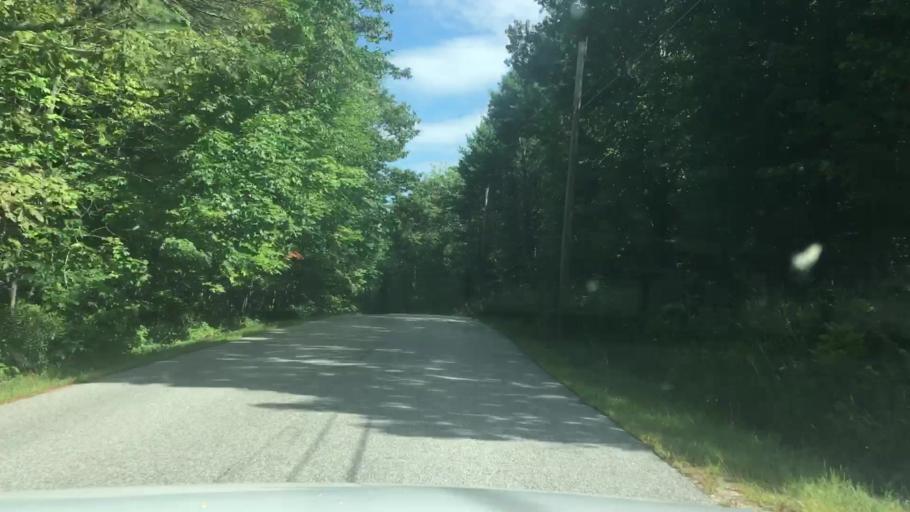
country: US
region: Maine
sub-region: Androscoggin County
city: Turner
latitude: 44.1865
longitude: -70.2615
